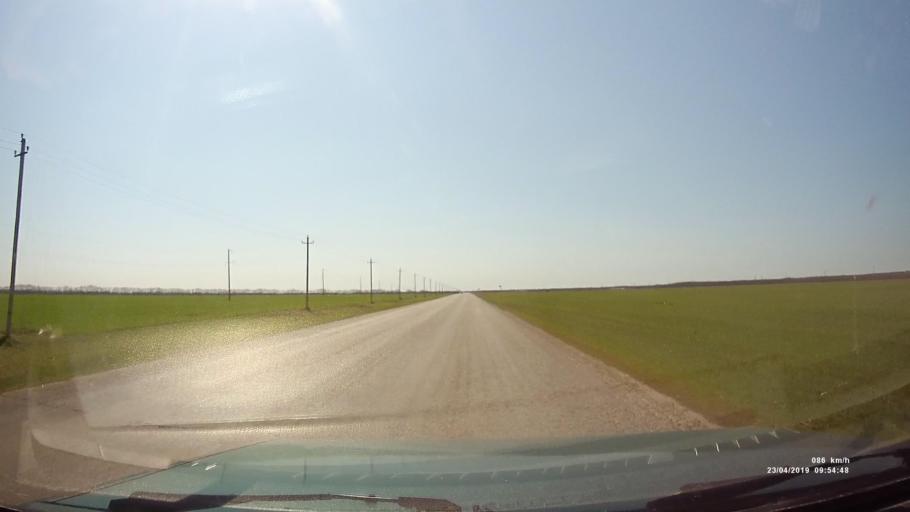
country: RU
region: Rostov
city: Orlovskiy
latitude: 46.8165
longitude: 42.0580
